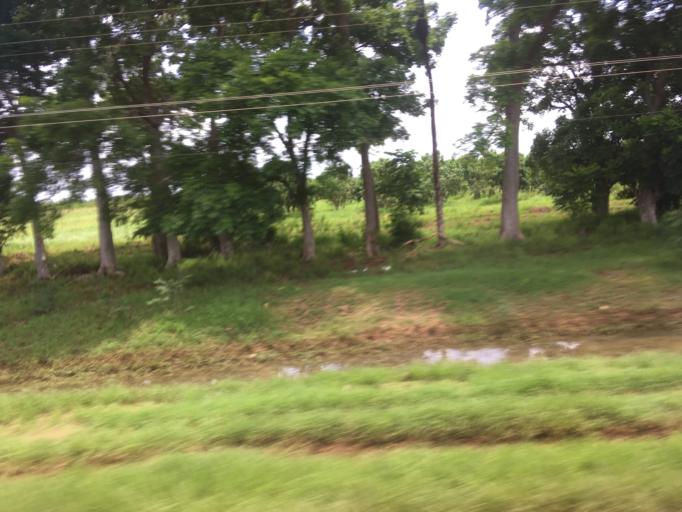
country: CU
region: Matanzas
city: Los Arabos
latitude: 22.7179
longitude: -80.6629
